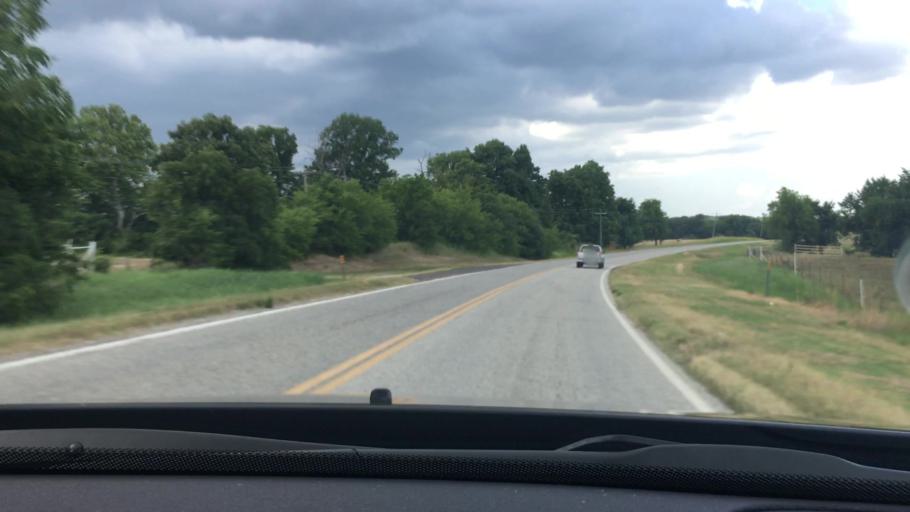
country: US
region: Oklahoma
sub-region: Pontotoc County
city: Ada
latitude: 34.5804
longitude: -96.6343
